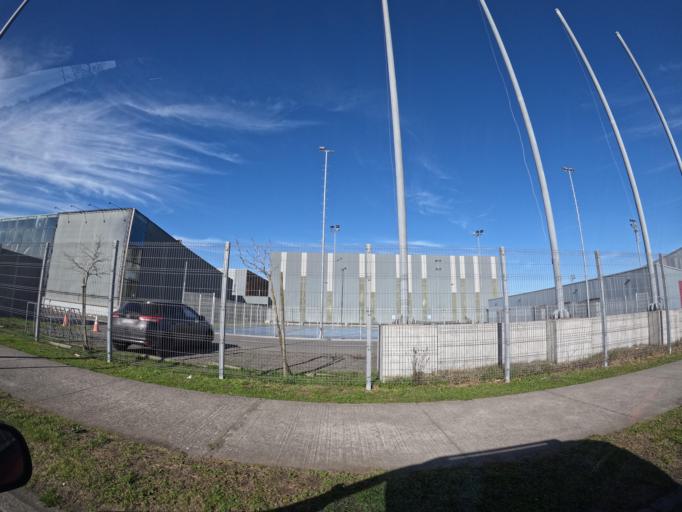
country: CL
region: Biobio
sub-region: Provincia de Concepcion
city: Concepcion
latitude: -36.7723
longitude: -73.0668
